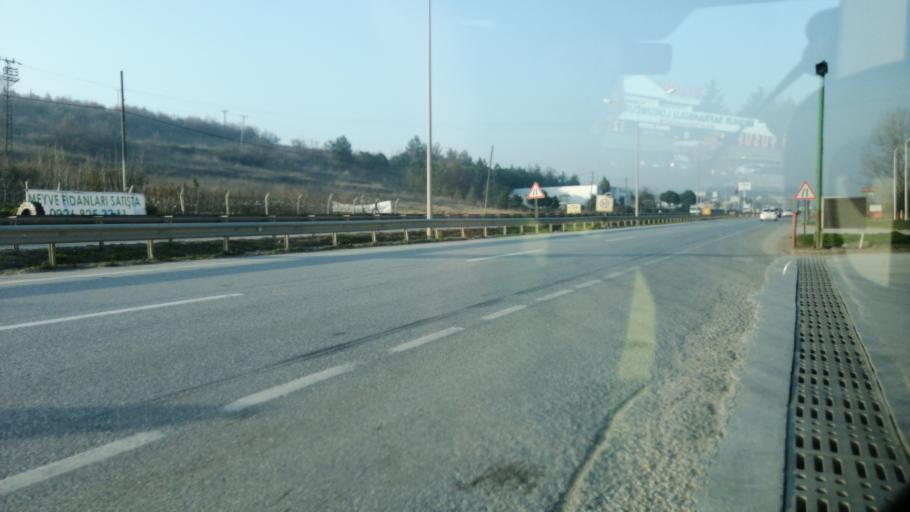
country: TR
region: Yalova
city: Yalova
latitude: 40.6247
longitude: 29.2711
